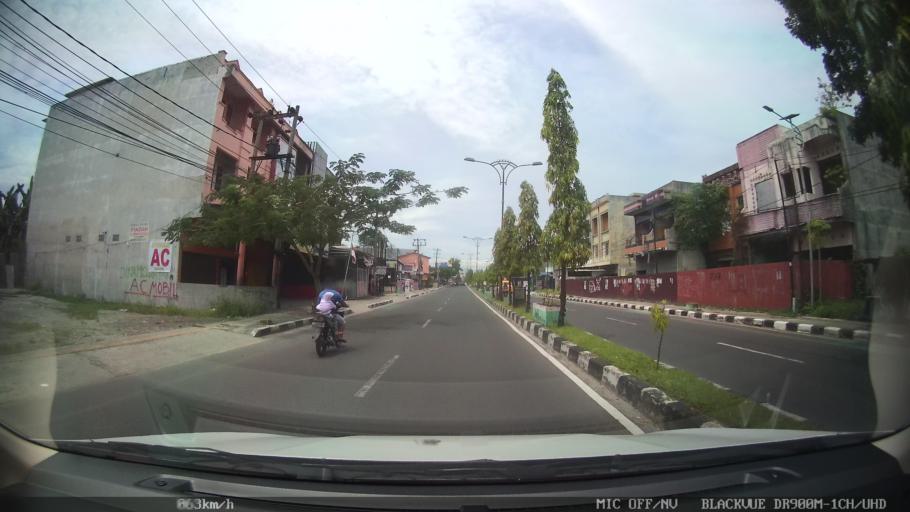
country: ID
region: North Sumatra
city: Sunggal
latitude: 3.5478
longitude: 98.6274
